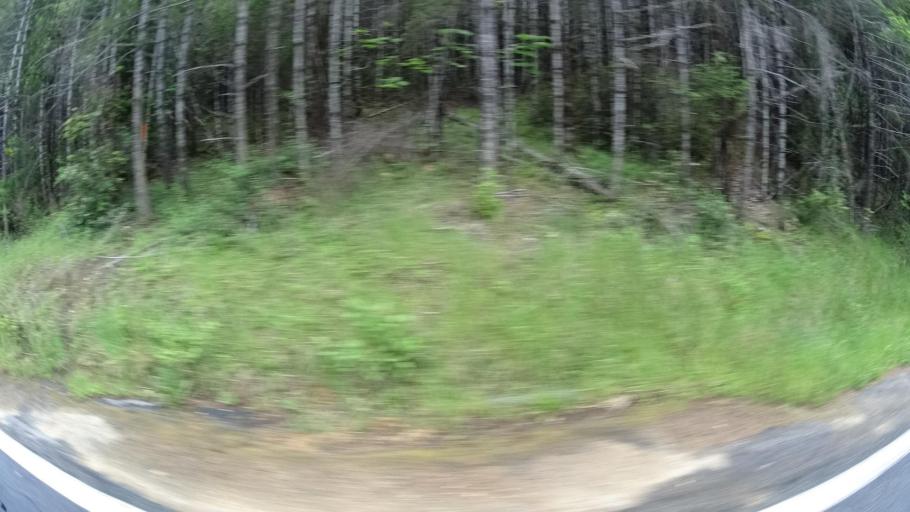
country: US
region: California
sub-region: Humboldt County
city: Willow Creek
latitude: 41.2670
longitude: -123.6066
